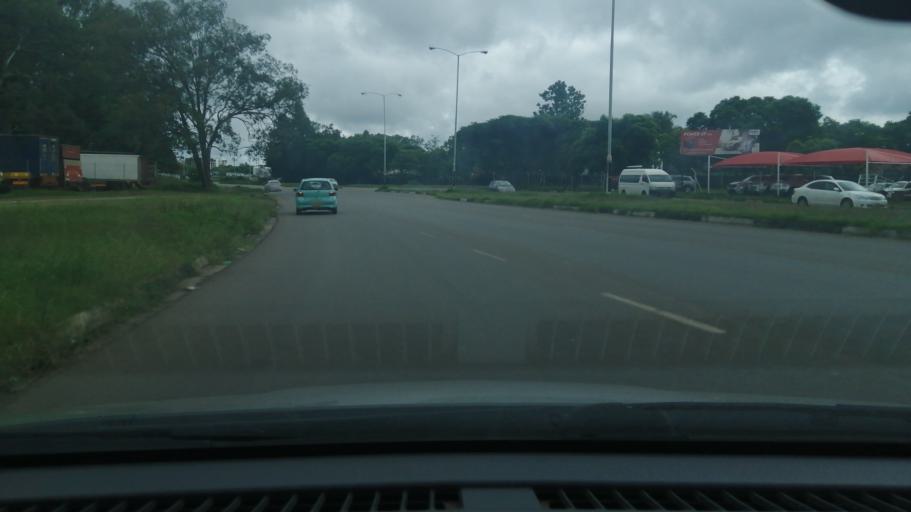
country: ZW
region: Harare
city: Harare
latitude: -17.8292
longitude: 31.0611
